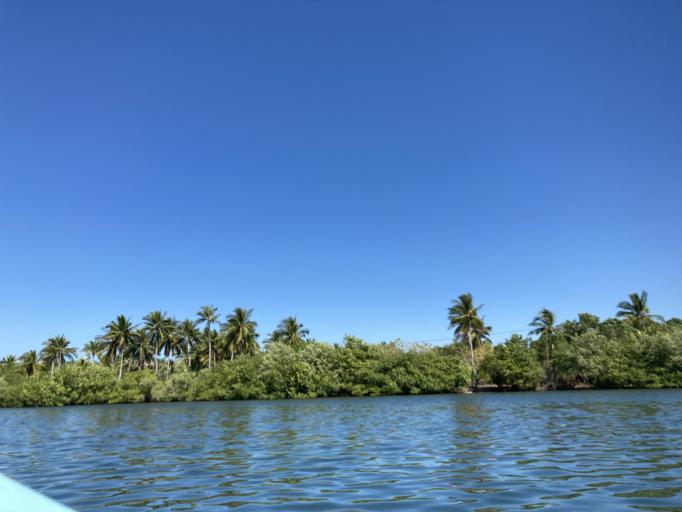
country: GT
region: Jutiapa
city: Pasaco
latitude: 13.8088
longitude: -90.2712
